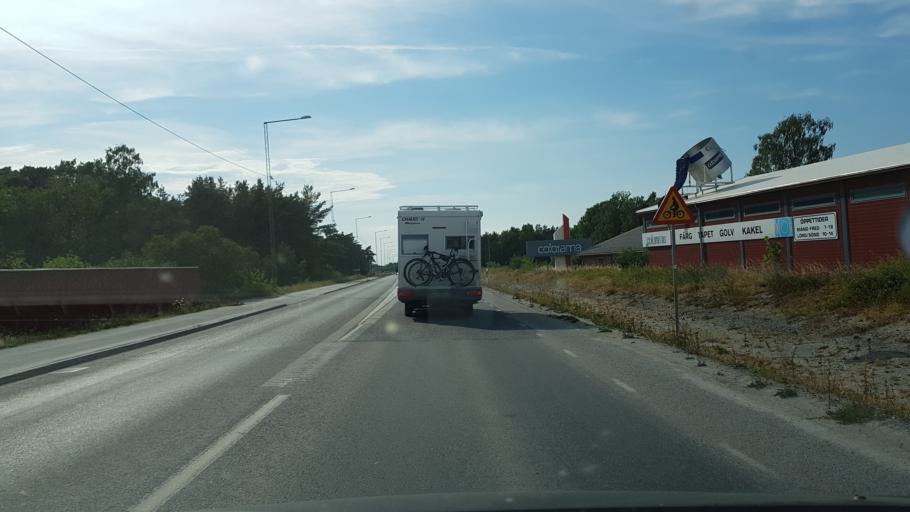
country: SE
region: Gotland
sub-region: Gotland
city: Visby
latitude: 57.6312
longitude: 18.3374
